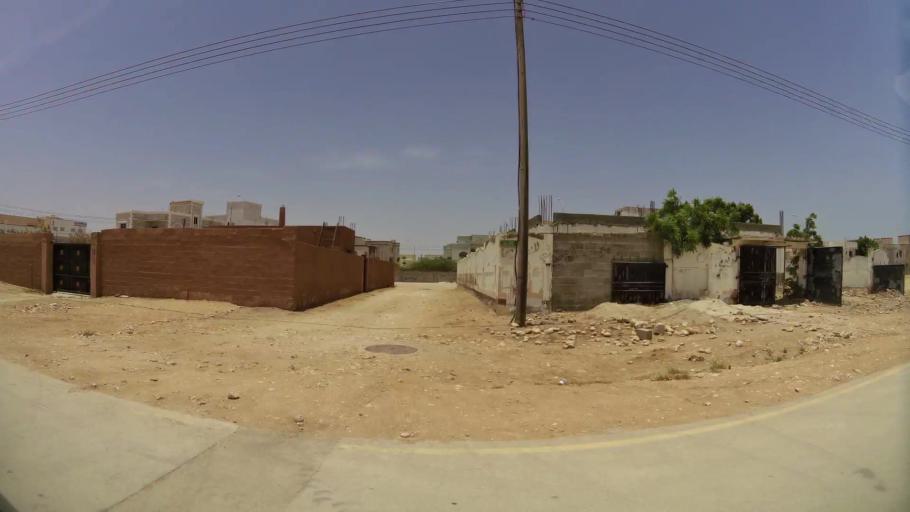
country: OM
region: Zufar
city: Salalah
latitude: 17.0831
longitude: 54.1551
